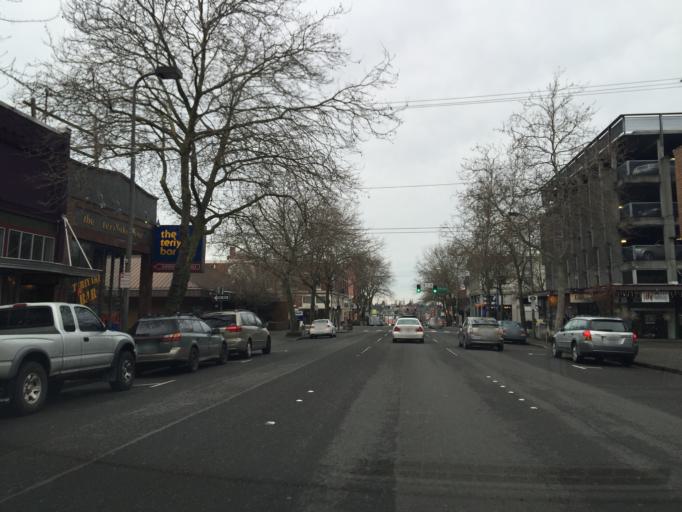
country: US
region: Washington
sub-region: Whatcom County
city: Bellingham
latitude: 48.7499
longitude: -122.4793
